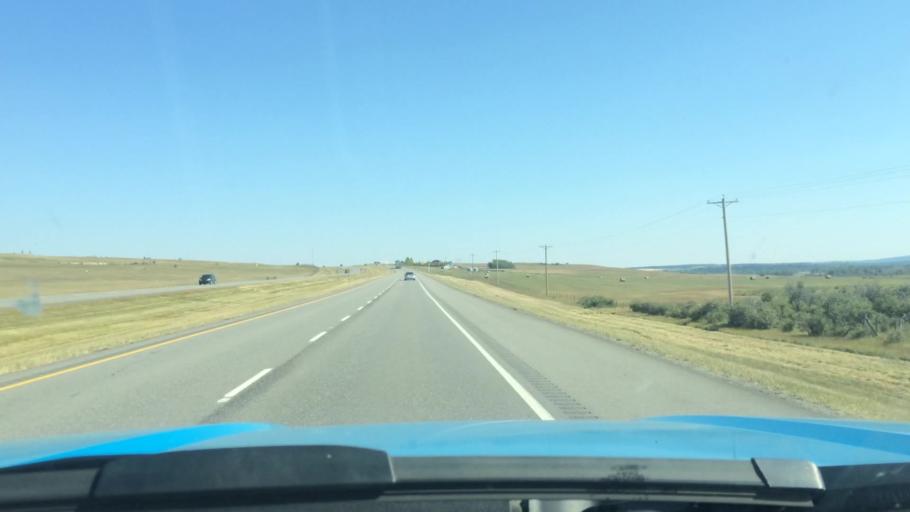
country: CA
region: Alberta
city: Cochrane
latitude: 51.0929
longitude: -114.5879
